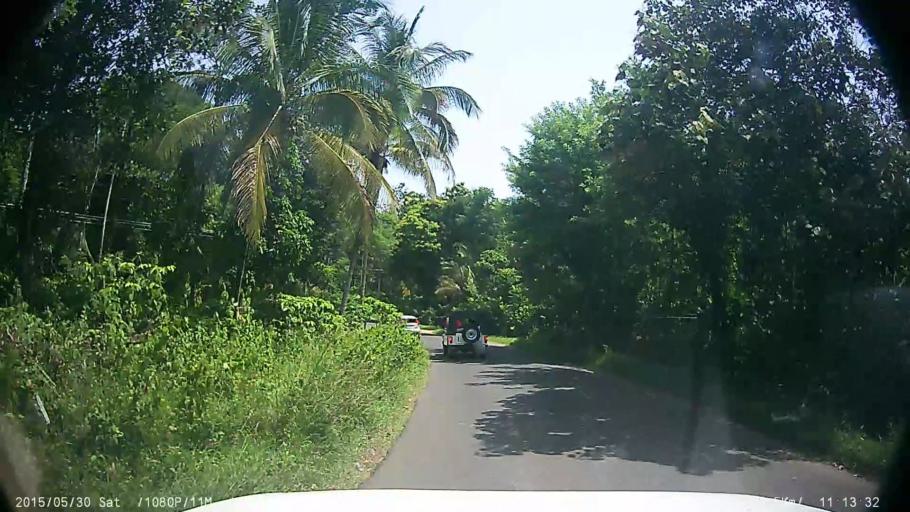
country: IN
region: Kerala
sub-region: Wayanad
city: Panamaram
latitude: 11.7621
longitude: 76.0634
